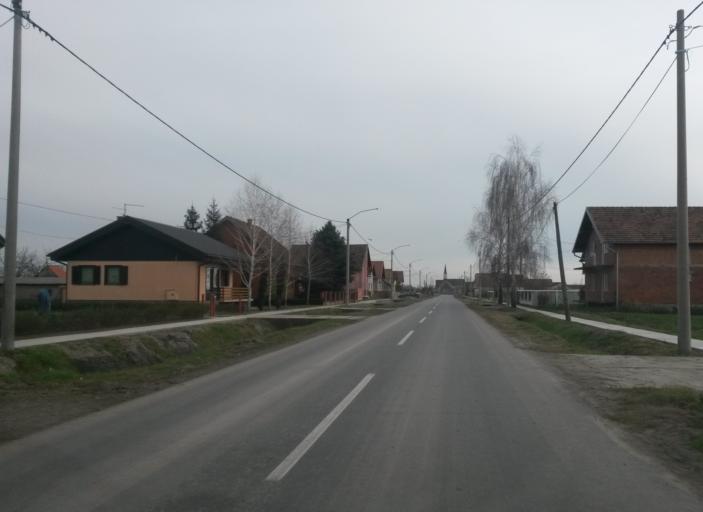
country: HR
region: Osjecko-Baranjska
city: Antunovac
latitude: 45.4901
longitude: 18.6283
